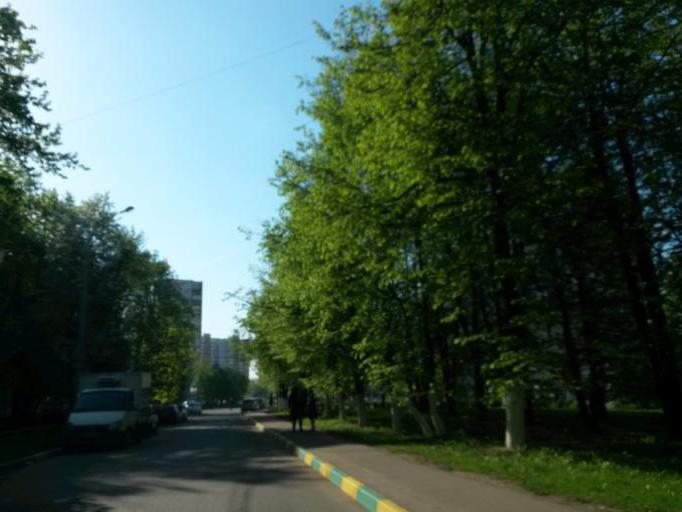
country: RU
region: Moskovskaya
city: Razvilka
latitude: 55.5898
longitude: 37.7524
